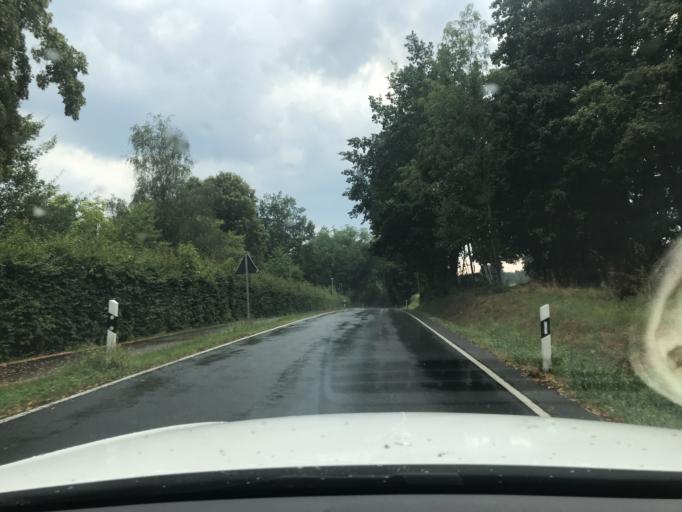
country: DE
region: Bavaria
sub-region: Upper Palatinate
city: Speinshart
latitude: 49.7560
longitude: 11.8129
